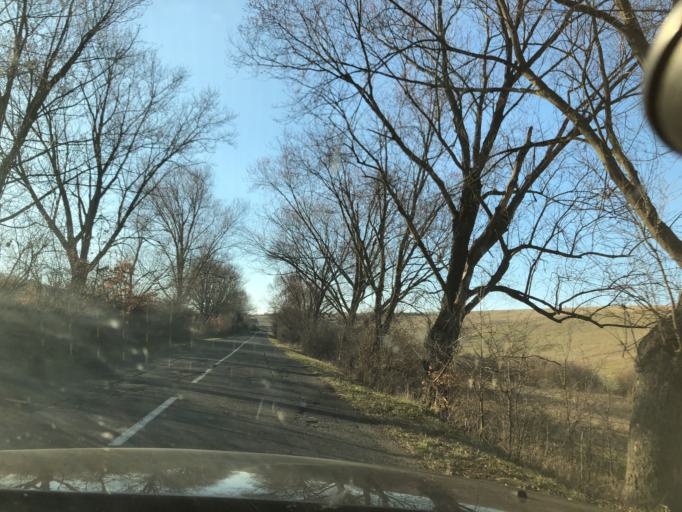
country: HU
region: Nograd
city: Rimoc
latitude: 47.9918
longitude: 19.6104
